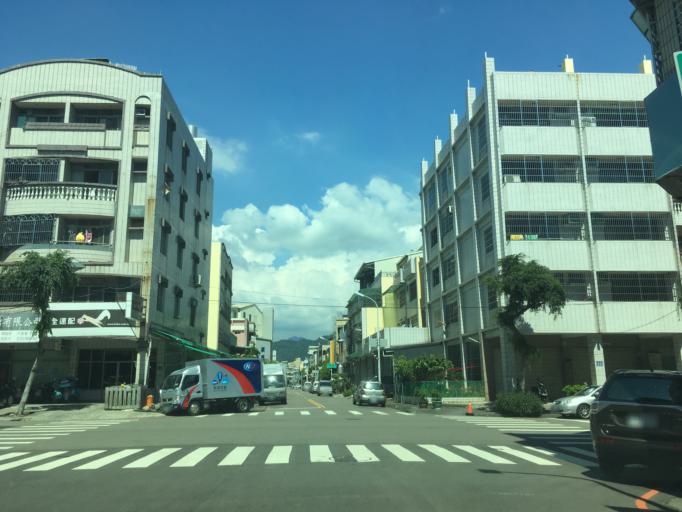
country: TW
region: Taiwan
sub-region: Taichung City
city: Taichung
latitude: 24.1422
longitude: 120.7057
